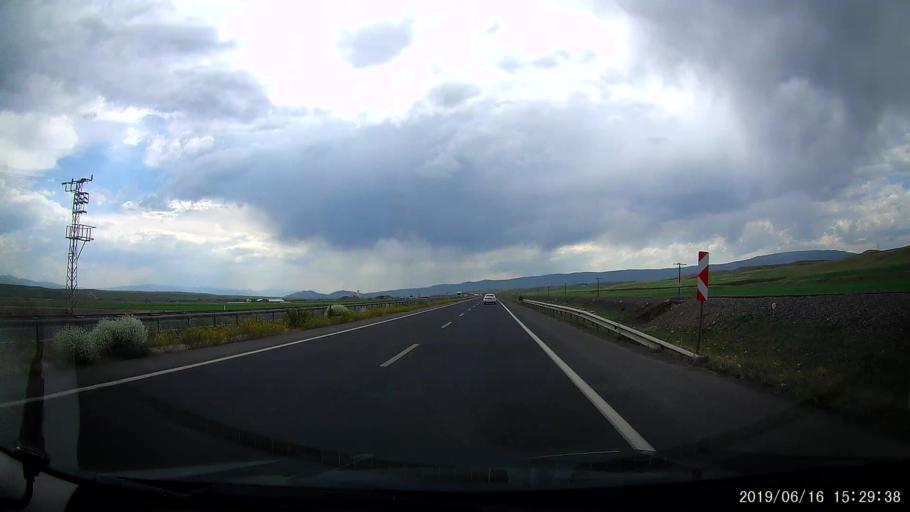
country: TR
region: Erzurum
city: Horasan
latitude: 40.0322
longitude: 42.1269
